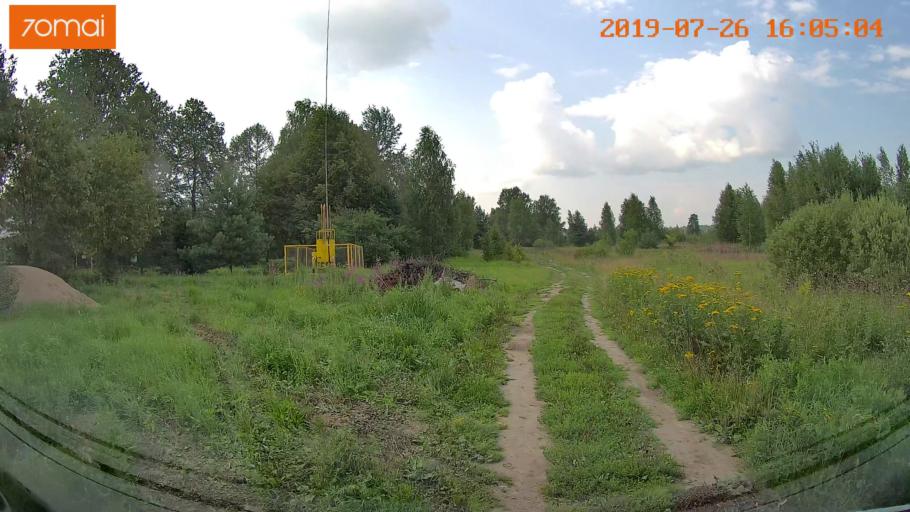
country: RU
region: Ivanovo
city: Bogorodskoye
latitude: 57.0576
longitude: 41.0578
